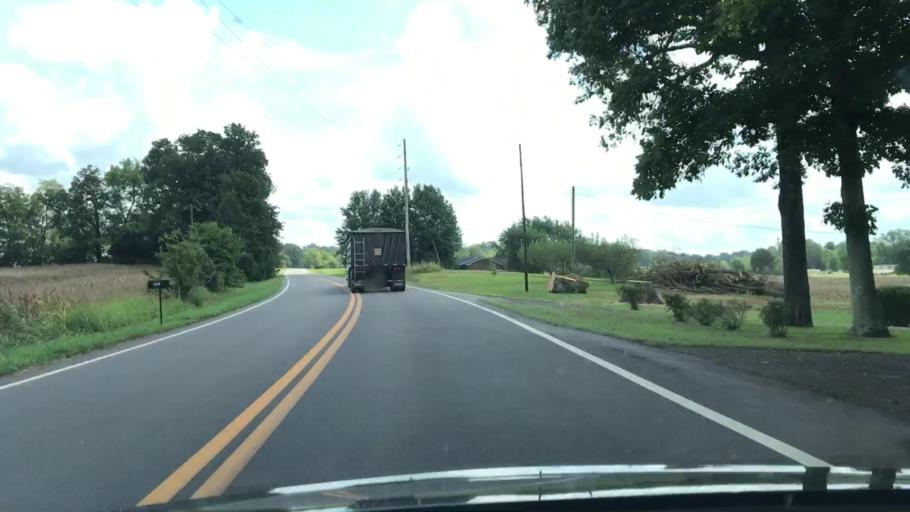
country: US
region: Tennessee
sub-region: Robertson County
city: Springfield
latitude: 36.6223
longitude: -86.9486
